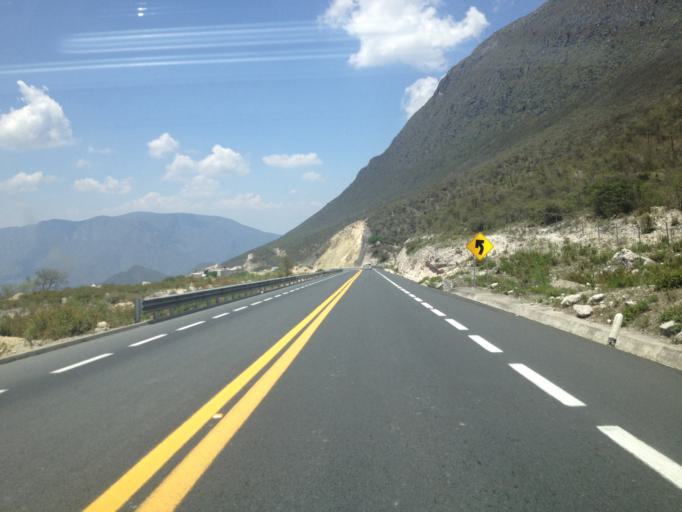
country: MX
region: Puebla
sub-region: San Jose Miahuatlan
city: San Pedro Tetitlan
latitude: 18.0612
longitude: -97.3541
